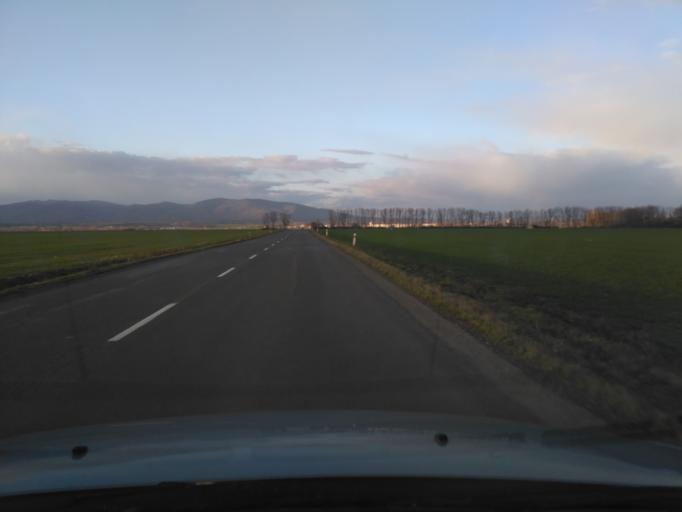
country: SK
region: Kosicky
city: Secovce
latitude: 48.6678
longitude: 21.6615
